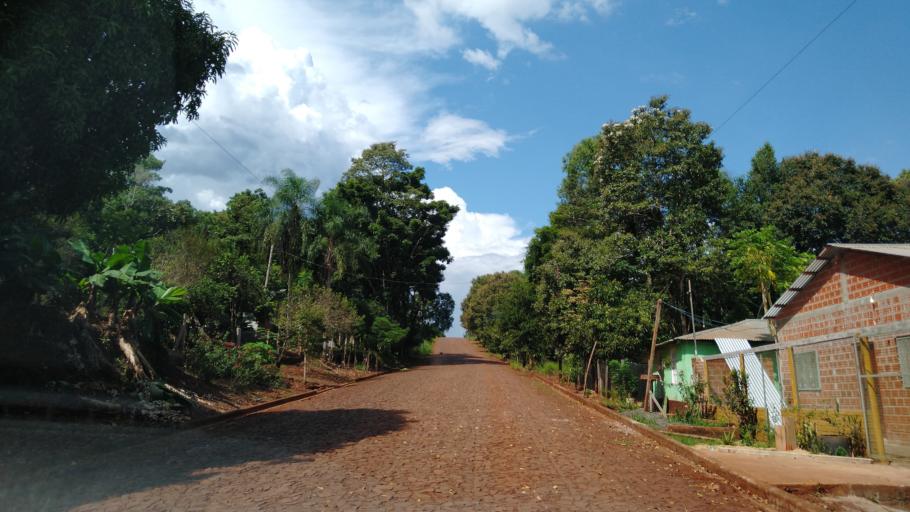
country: AR
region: Misiones
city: Puerto Libertad
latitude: -25.9659
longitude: -54.5997
